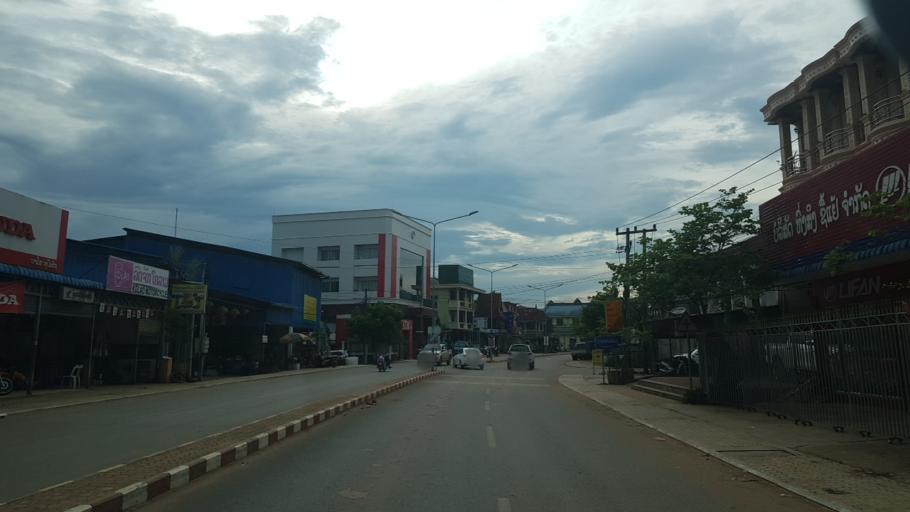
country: LA
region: Oudomxai
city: Muang Xay
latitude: 20.6888
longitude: 101.9855
